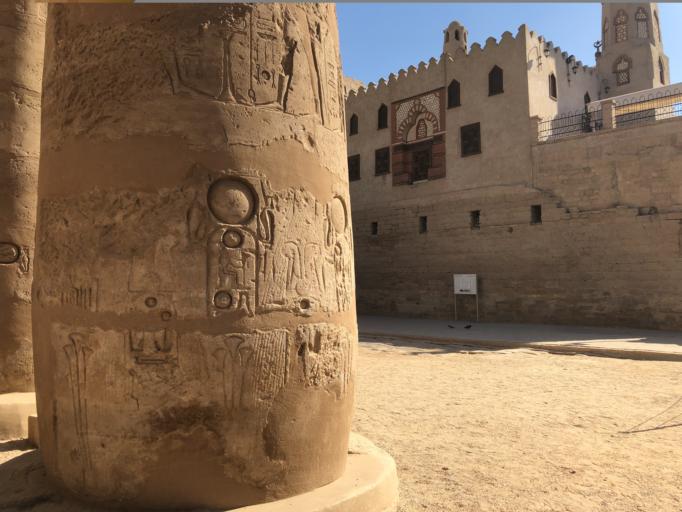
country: EG
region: Luxor
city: Luxor
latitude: 25.7001
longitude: 32.6392
